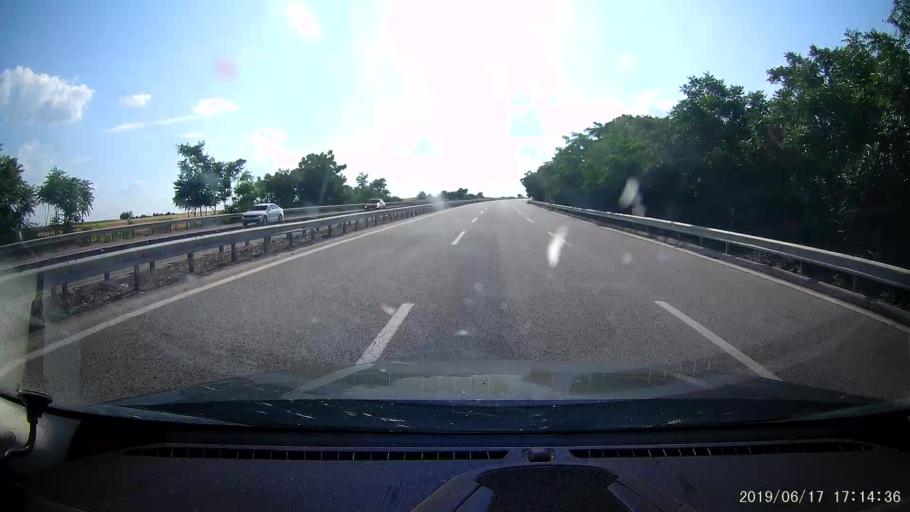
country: TR
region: Edirne
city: Edirne
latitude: 41.6994
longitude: 26.5146
